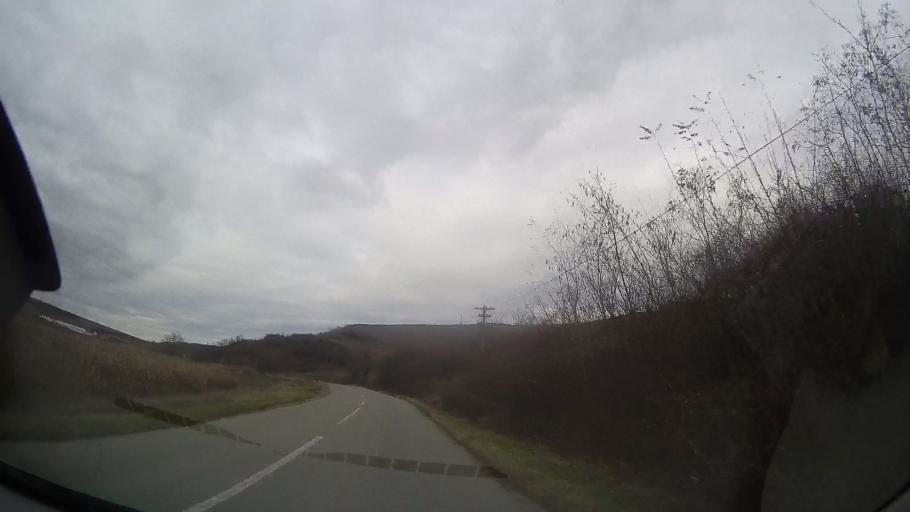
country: RO
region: Mures
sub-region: Comuna Faragau
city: Faragau
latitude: 46.7515
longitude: 24.5258
